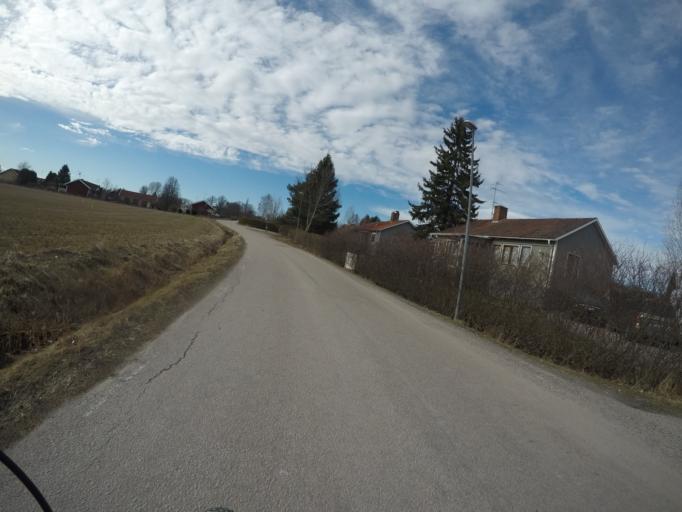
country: SE
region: Vaestmanland
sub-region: Kungsors Kommun
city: Kungsoer
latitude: 59.4180
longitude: 16.1948
